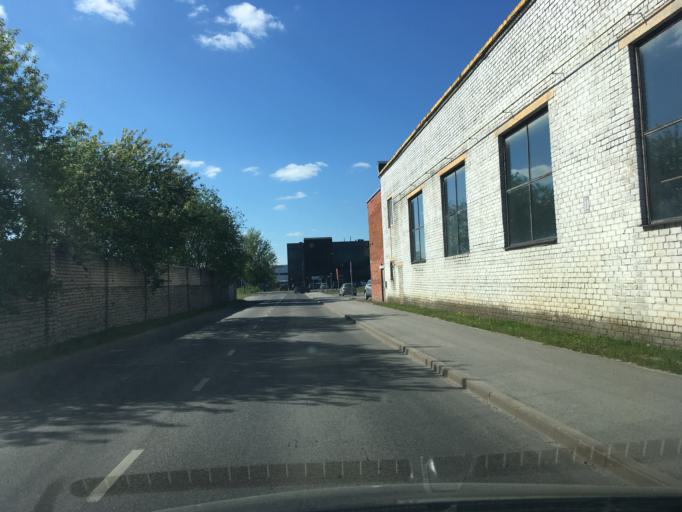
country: EE
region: Harju
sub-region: Tallinna linn
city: Tallinn
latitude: 59.4214
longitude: 24.8110
